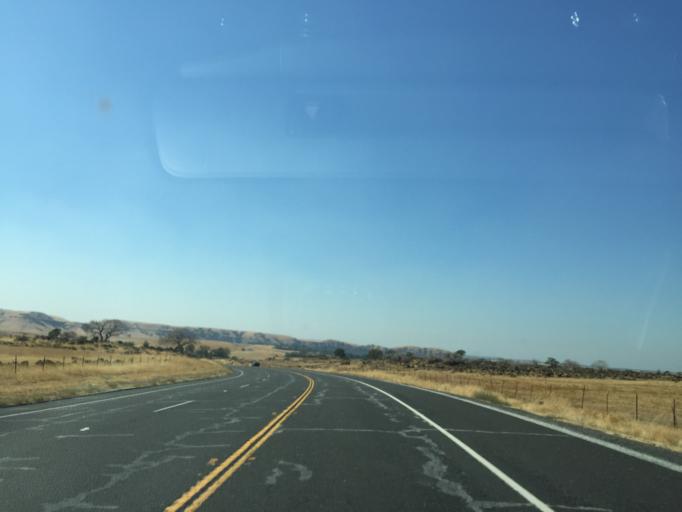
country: US
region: California
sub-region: Stanislaus County
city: East Oakdale
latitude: 37.8206
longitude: -120.6494
